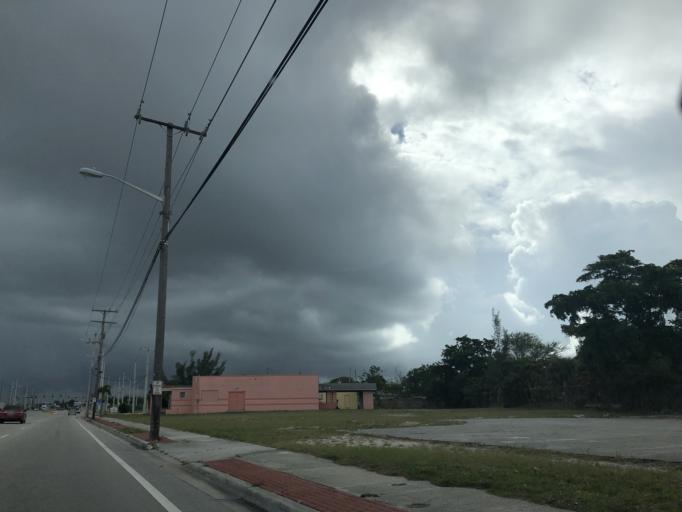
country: US
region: Florida
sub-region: Palm Beach County
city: Riviera Beach
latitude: 26.7720
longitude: -80.0627
